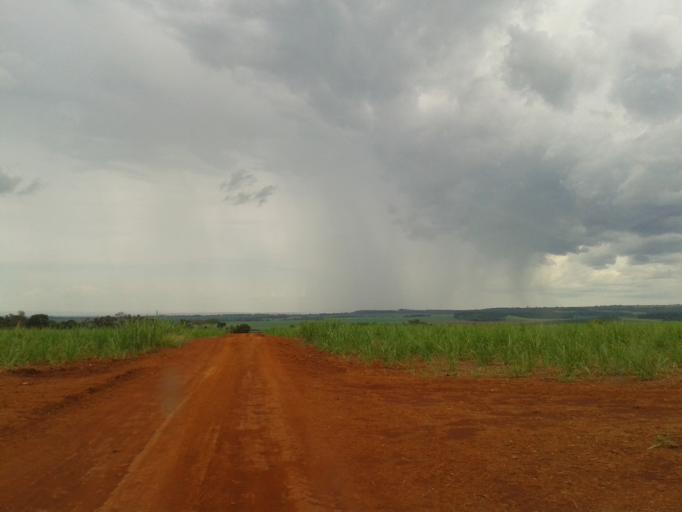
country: BR
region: Minas Gerais
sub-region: Centralina
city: Centralina
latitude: -18.6668
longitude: -49.2600
